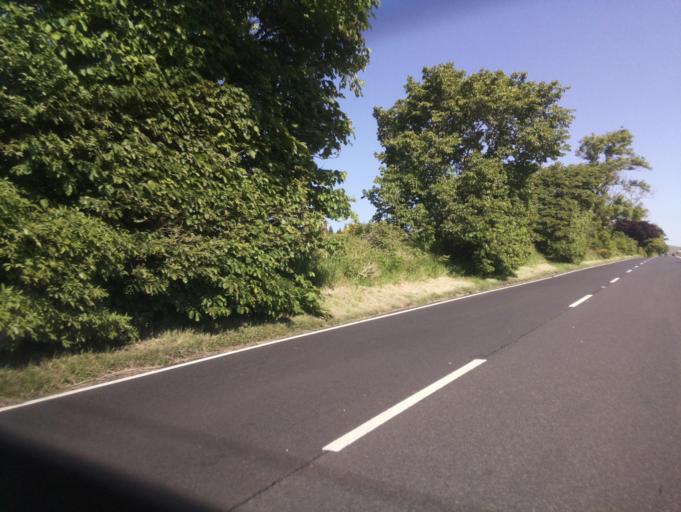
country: GB
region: Scotland
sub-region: Fife
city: Balmullo
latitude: 56.3519
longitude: -2.9415
